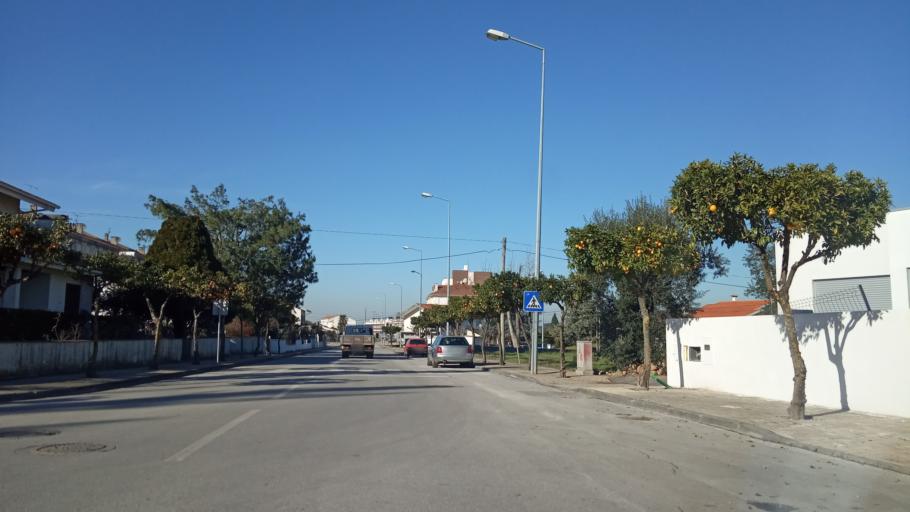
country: PT
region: Aveiro
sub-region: Anadia
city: Anadia
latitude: 40.4397
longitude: -8.4325
